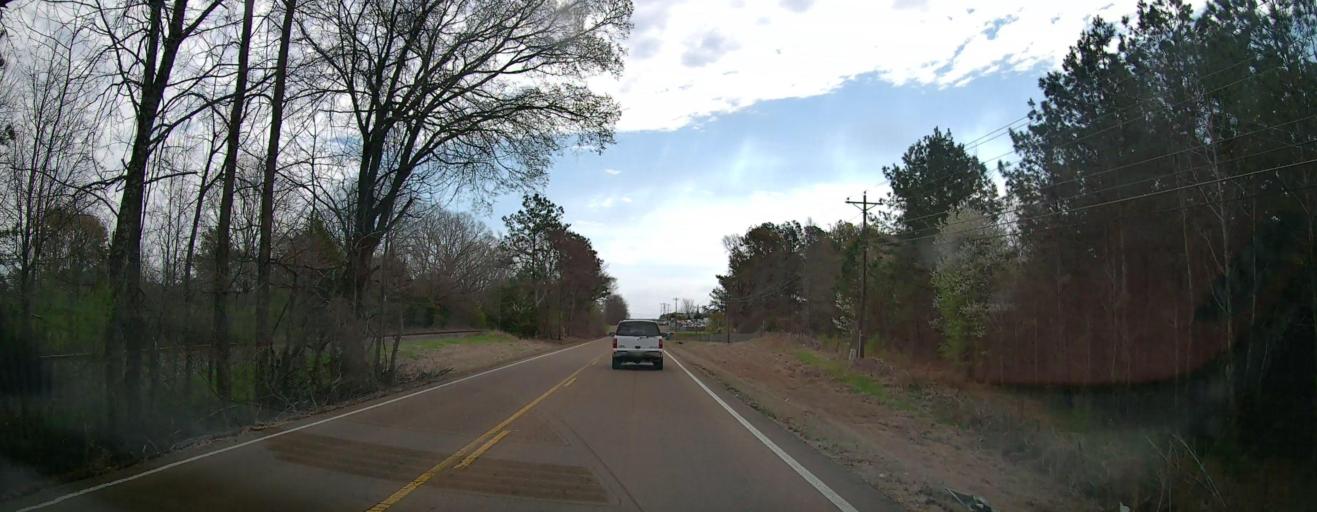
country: US
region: Mississippi
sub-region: Marshall County
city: Byhalia
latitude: 34.8872
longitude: -89.7263
